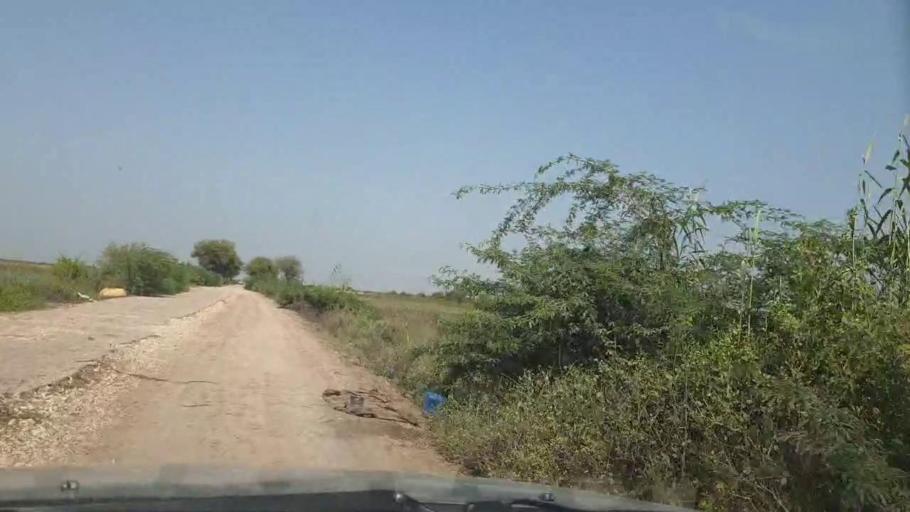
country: PK
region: Sindh
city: Tando Ghulam Ali
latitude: 25.1088
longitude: 68.8021
